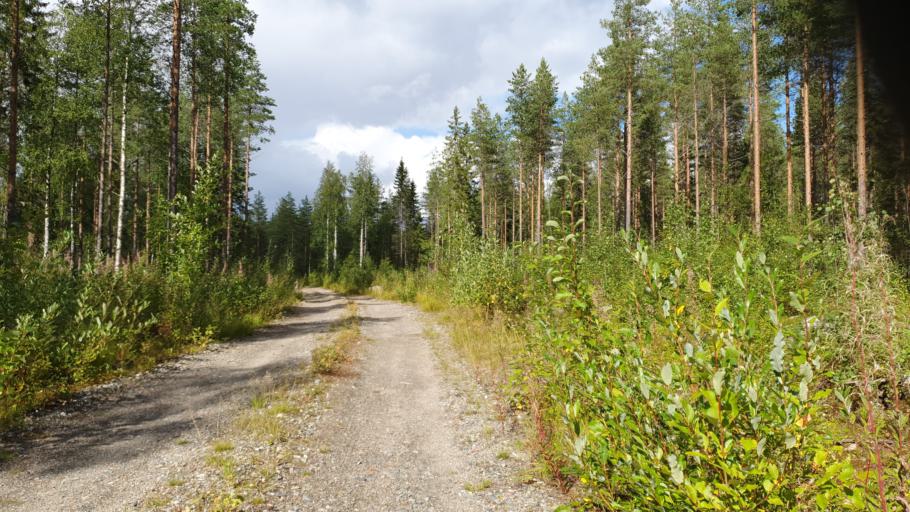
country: FI
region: Kainuu
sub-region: Kehys-Kainuu
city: Kuhmo
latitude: 64.1402
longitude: 29.3884
